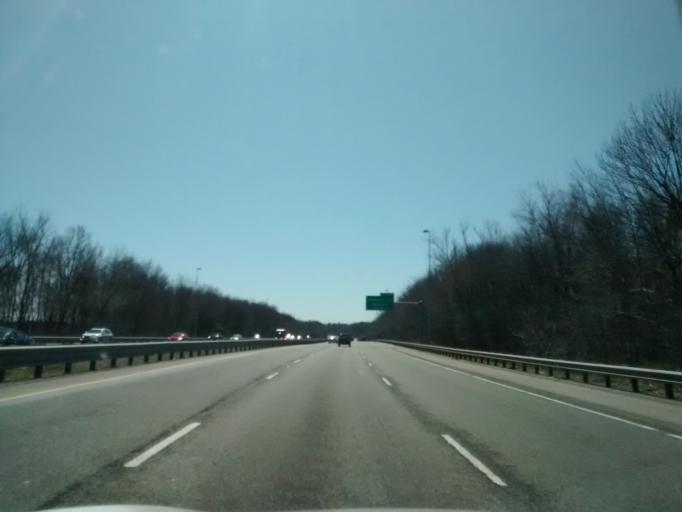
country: US
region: Massachusetts
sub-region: Worcester County
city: Auburn
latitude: 42.2184
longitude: -71.8298
